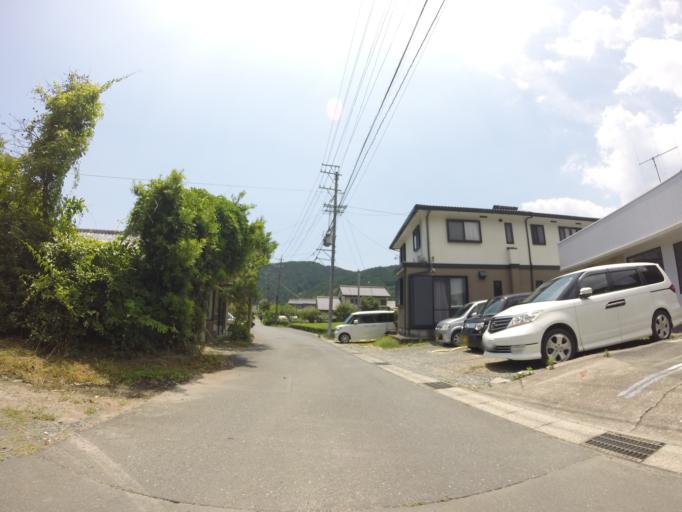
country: JP
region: Shizuoka
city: Kanaya
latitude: 34.8065
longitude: 138.0729
